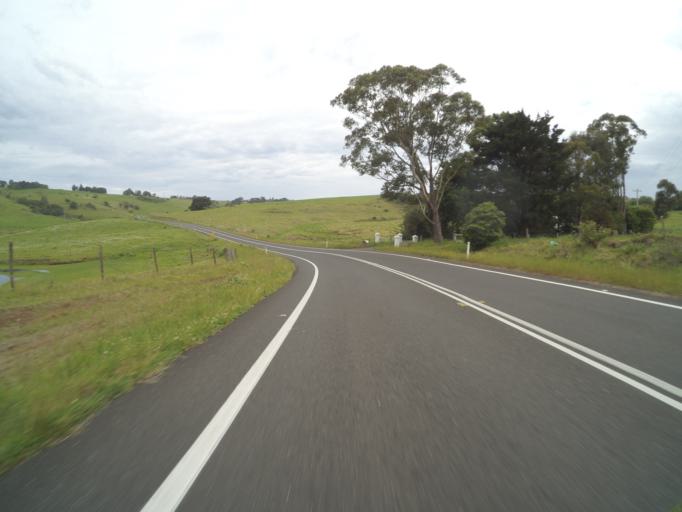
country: AU
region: New South Wales
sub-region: Kiama
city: Kiama
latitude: -34.6606
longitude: 150.8225
